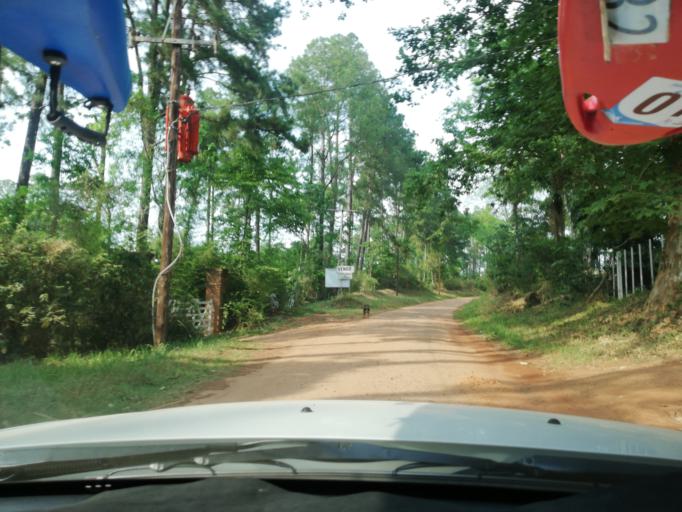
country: AR
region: Misiones
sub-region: Departamento de San Ignacio
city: San Ignacio
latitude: -27.2927
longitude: -55.5640
